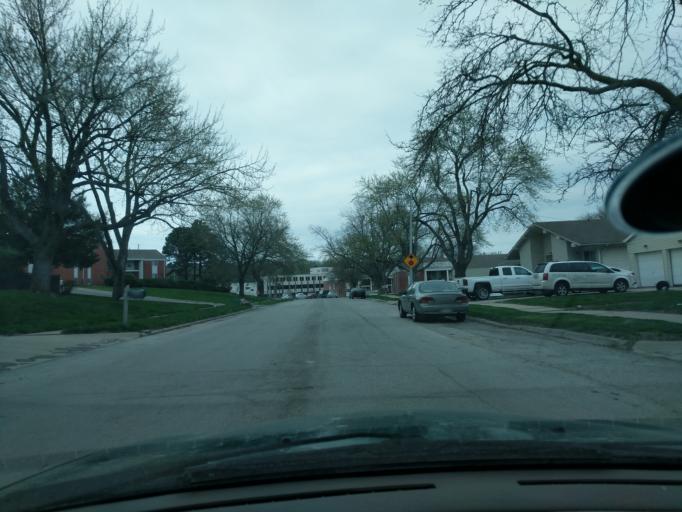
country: US
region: Nebraska
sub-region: Douglas County
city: Ralston
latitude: 41.2326
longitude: -96.0942
